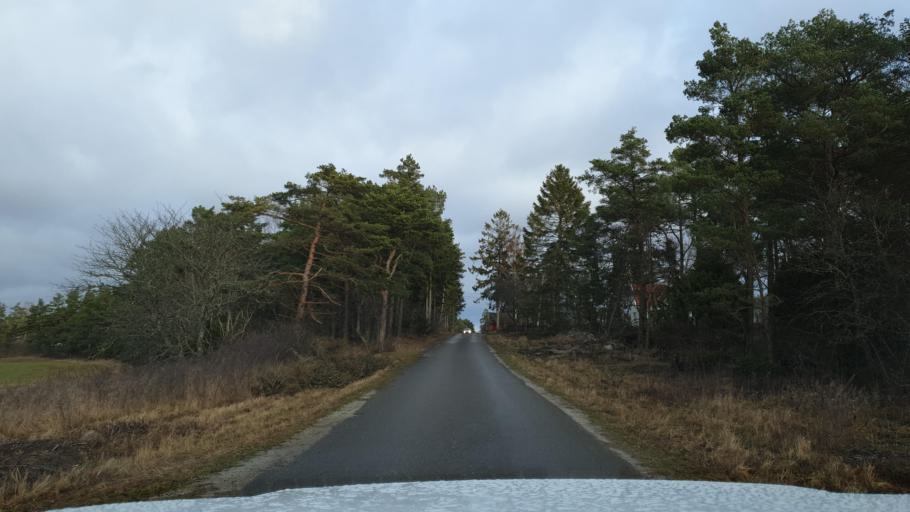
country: SE
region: Gotland
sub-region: Gotland
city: Slite
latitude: 57.3775
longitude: 18.8030
